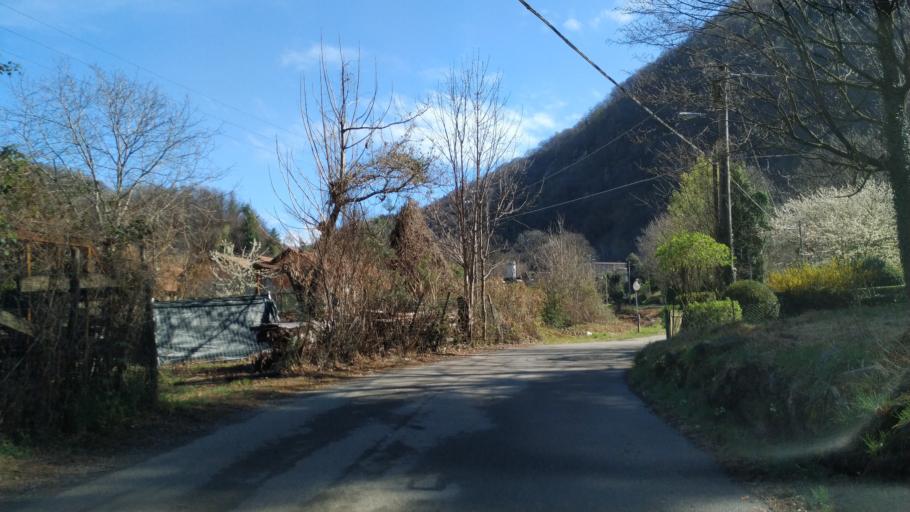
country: IT
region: Piedmont
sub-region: Provincia di Vercelli
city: Civiasco
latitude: 45.7942
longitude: 8.2791
